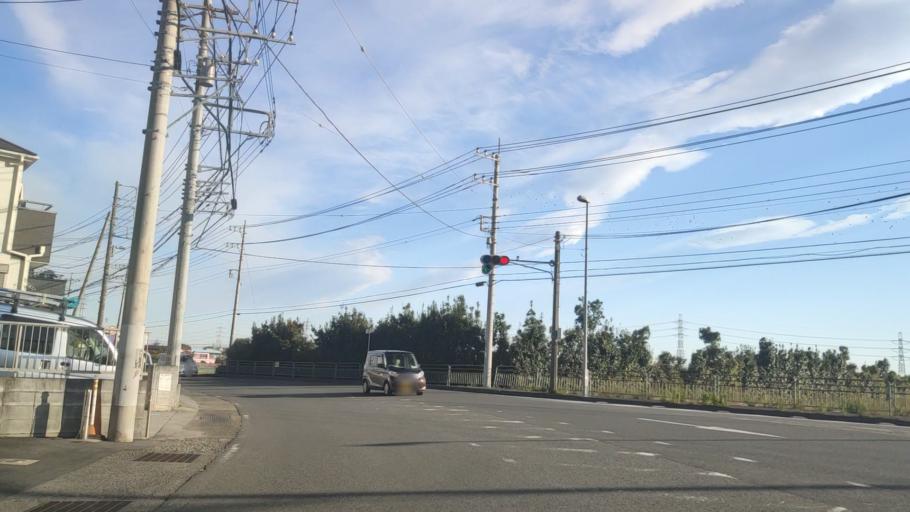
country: JP
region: Kanagawa
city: Atsugi
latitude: 35.4216
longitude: 139.3881
